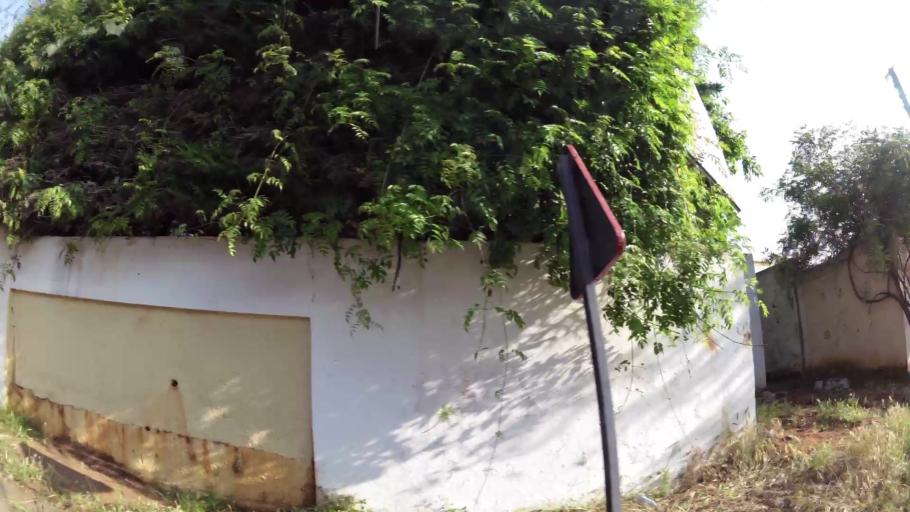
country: MA
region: Rabat-Sale-Zemmour-Zaer
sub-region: Rabat
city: Rabat
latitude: 33.9415
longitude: -6.8142
